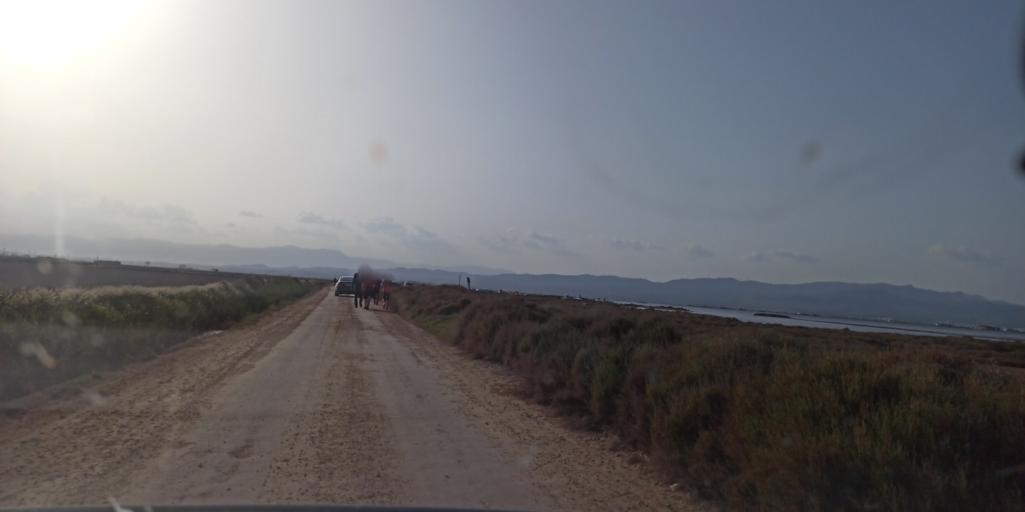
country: ES
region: Catalonia
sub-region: Provincia de Tarragona
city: Deltebre
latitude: 40.7632
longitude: 0.7531
